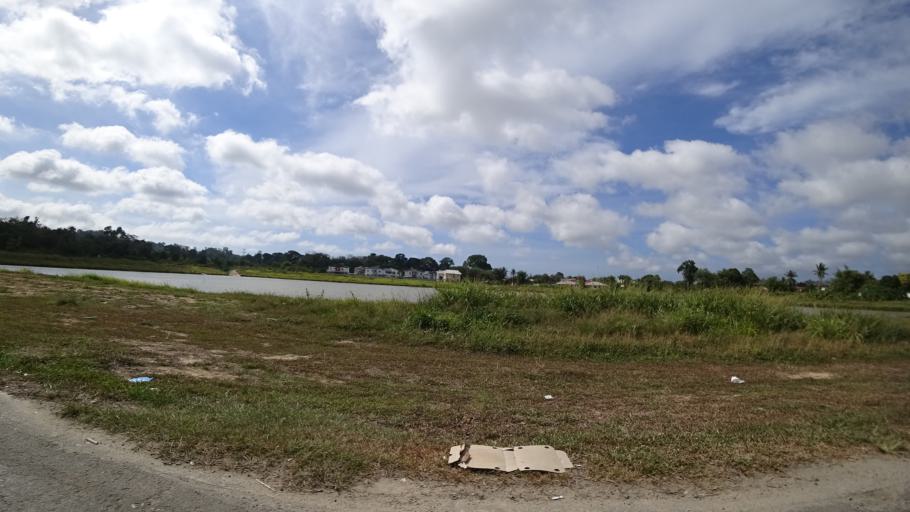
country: BN
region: Brunei and Muara
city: Bandar Seri Begawan
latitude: 4.8942
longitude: 114.8433
